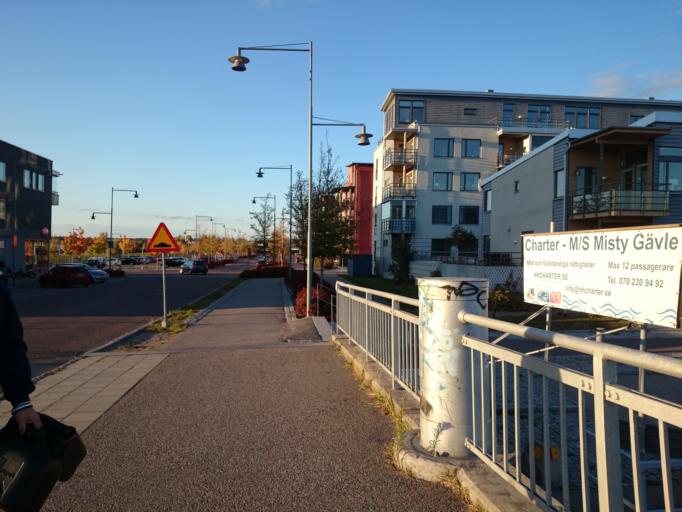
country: SE
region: Gaevleborg
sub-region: Gavle Kommun
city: Gavle
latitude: 60.6784
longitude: 17.1636
